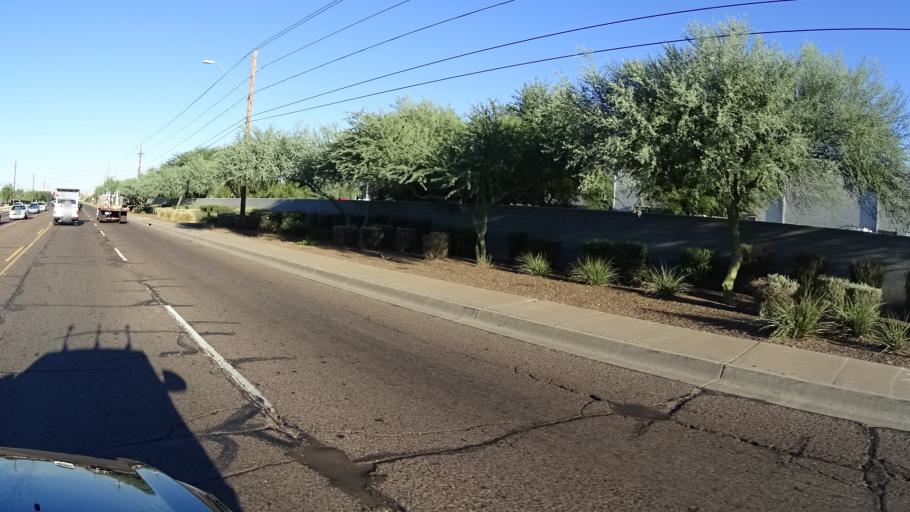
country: US
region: Arizona
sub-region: Maricopa County
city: Laveen
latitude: 33.4369
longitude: -112.1543
